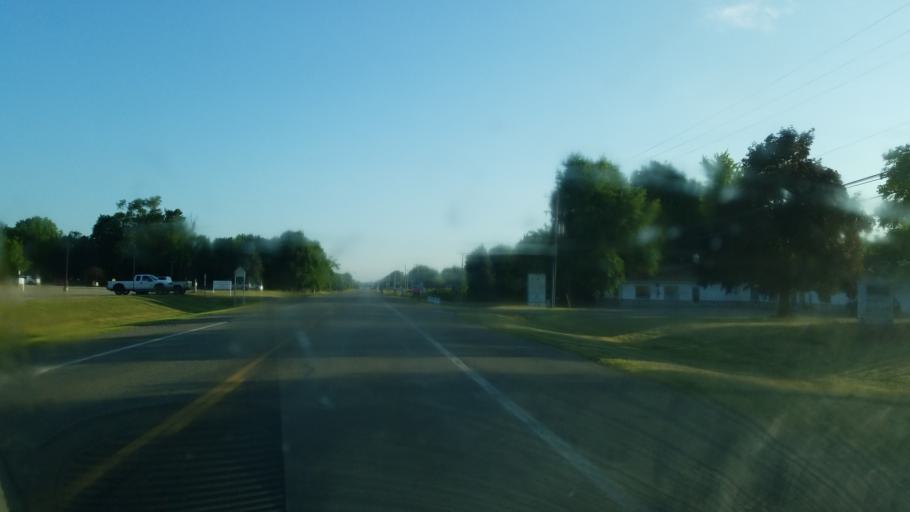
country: US
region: Michigan
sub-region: Montcalm County
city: Stanton
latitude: 43.3006
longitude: -85.0848
